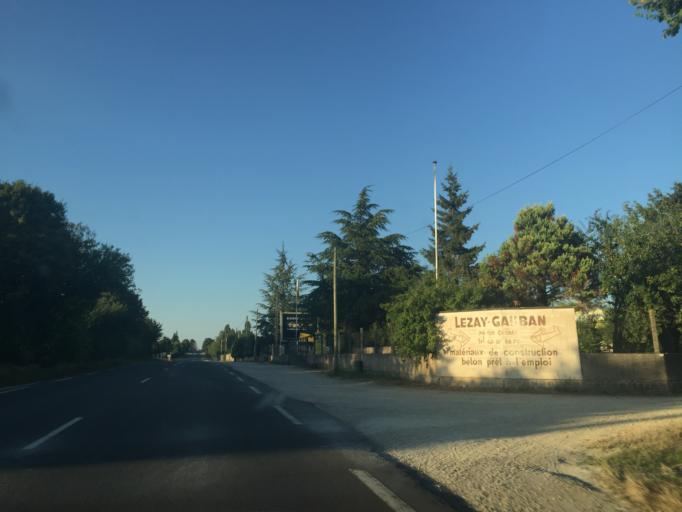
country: FR
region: Poitou-Charentes
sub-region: Departement des Deux-Sevres
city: Lezay
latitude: 46.3178
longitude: -0.0401
